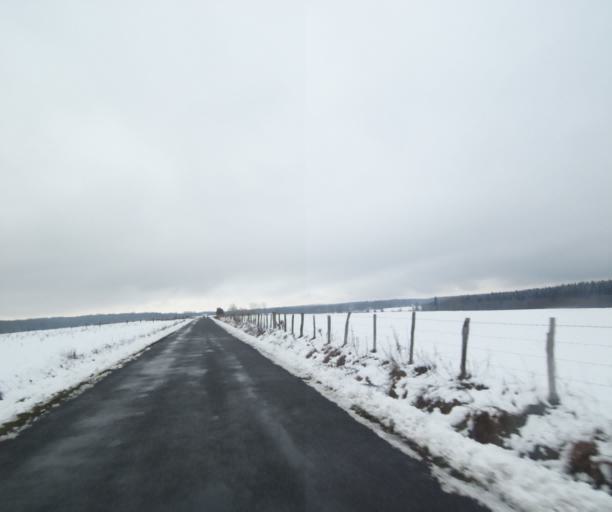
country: FR
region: Champagne-Ardenne
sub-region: Departement de la Haute-Marne
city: Laneuville-a-Remy
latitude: 48.4824
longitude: 4.8719
